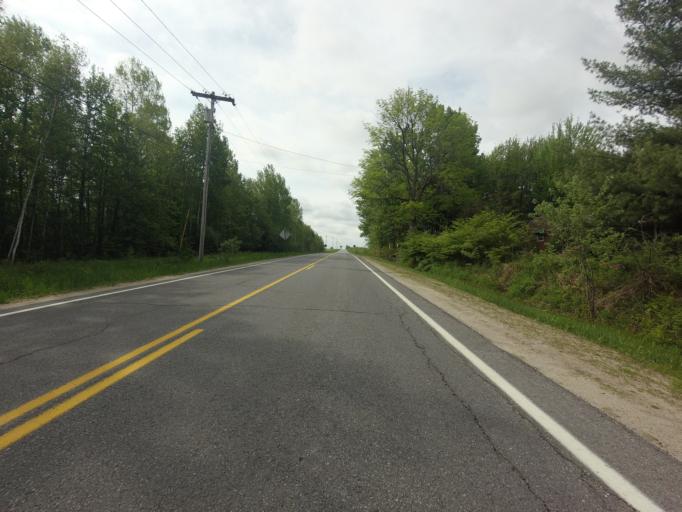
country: CA
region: Ontario
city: Cornwall
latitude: 44.7748
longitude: -74.6726
